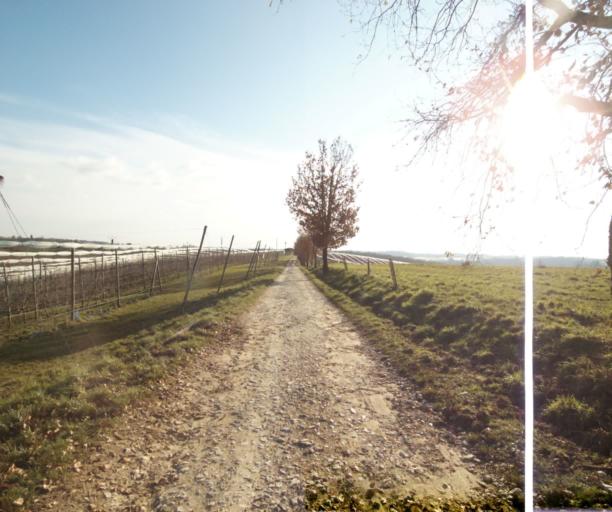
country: FR
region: Midi-Pyrenees
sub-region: Departement du Tarn-et-Garonne
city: Moissac
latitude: 44.1371
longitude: 1.0481
